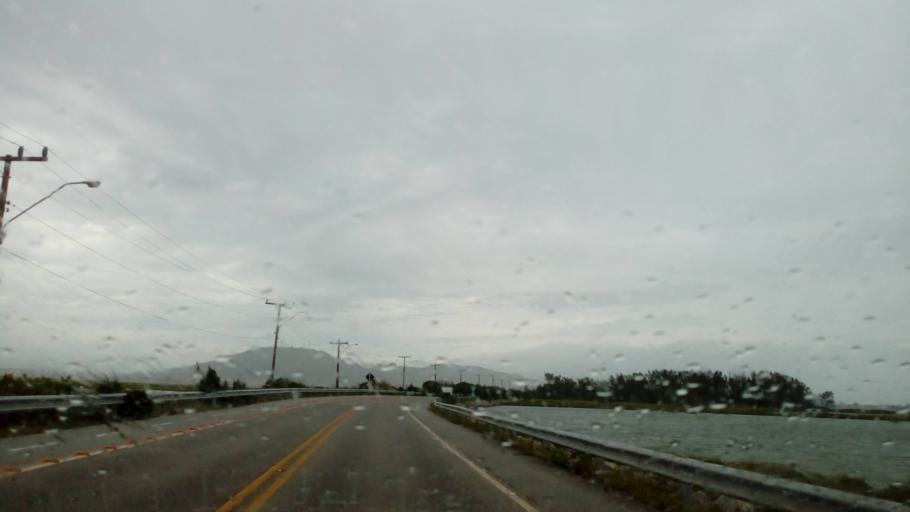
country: BR
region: Santa Catarina
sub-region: Laguna
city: Laguna
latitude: -28.5105
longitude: -48.7678
